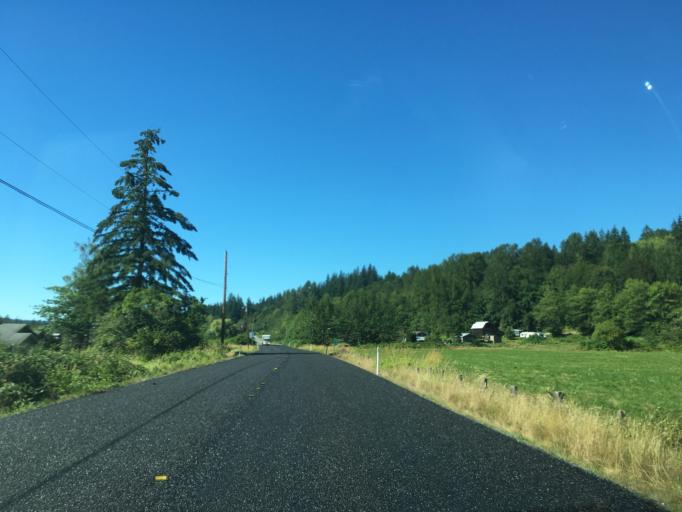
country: US
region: Washington
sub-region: Skagit County
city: Big Lake
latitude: 48.3590
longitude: -122.2041
